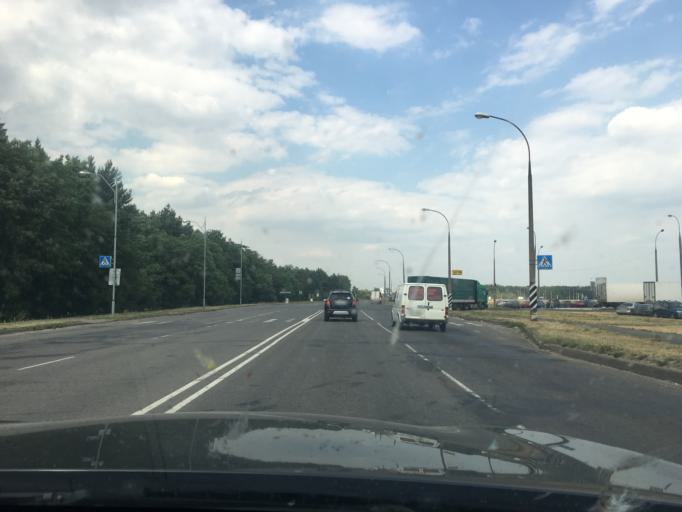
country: BY
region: Brest
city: Brest
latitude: 52.1479
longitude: 23.6865
